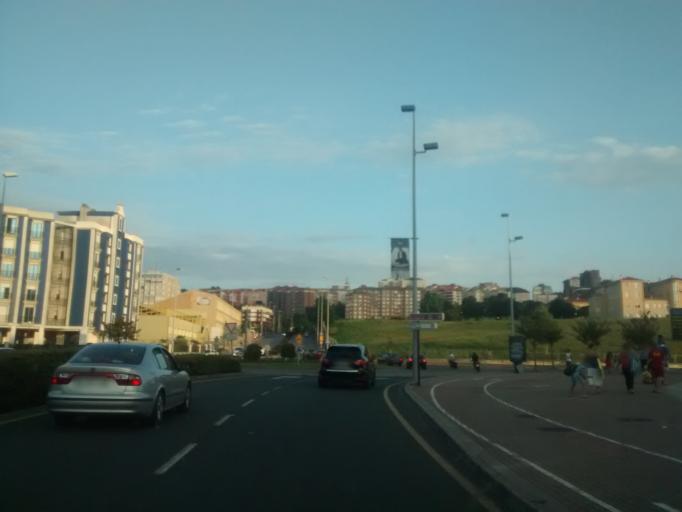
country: ES
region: Cantabria
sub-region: Provincia de Cantabria
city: Santander
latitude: 43.4755
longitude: -3.7948
